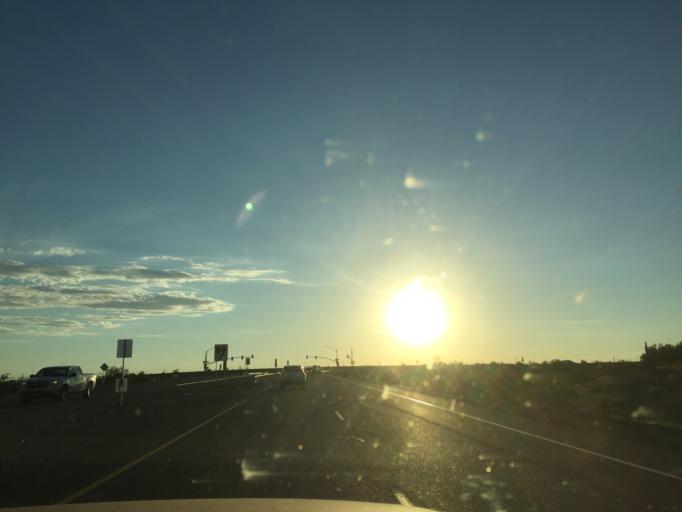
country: US
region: Arizona
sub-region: Maricopa County
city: Sun City West
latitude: 33.7138
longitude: -112.3038
